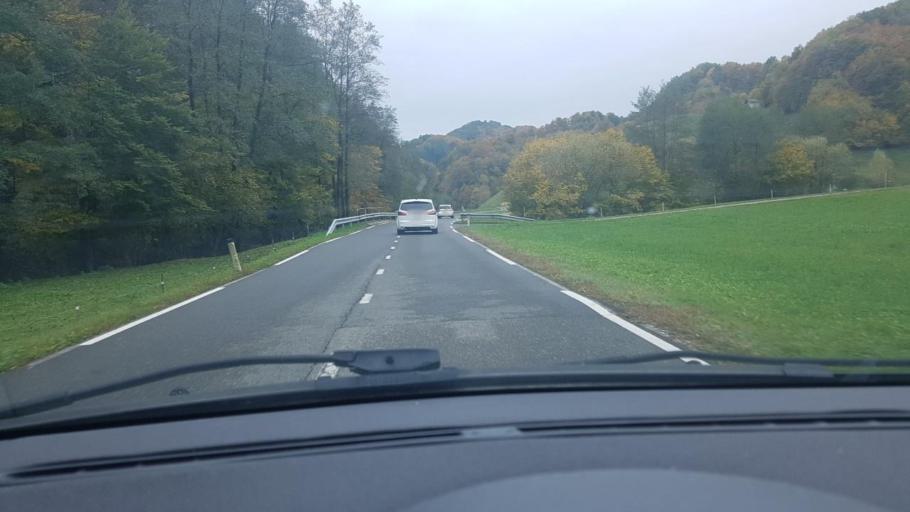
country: SI
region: Rogatec
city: Rogatec
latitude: 46.2836
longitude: 15.7129
